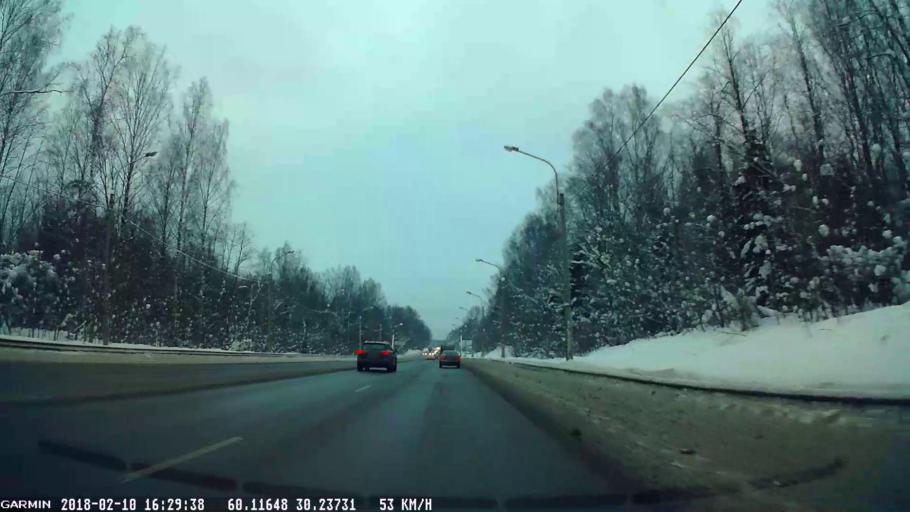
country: RU
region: St.-Petersburg
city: Levashovo
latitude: 60.1172
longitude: 30.2367
